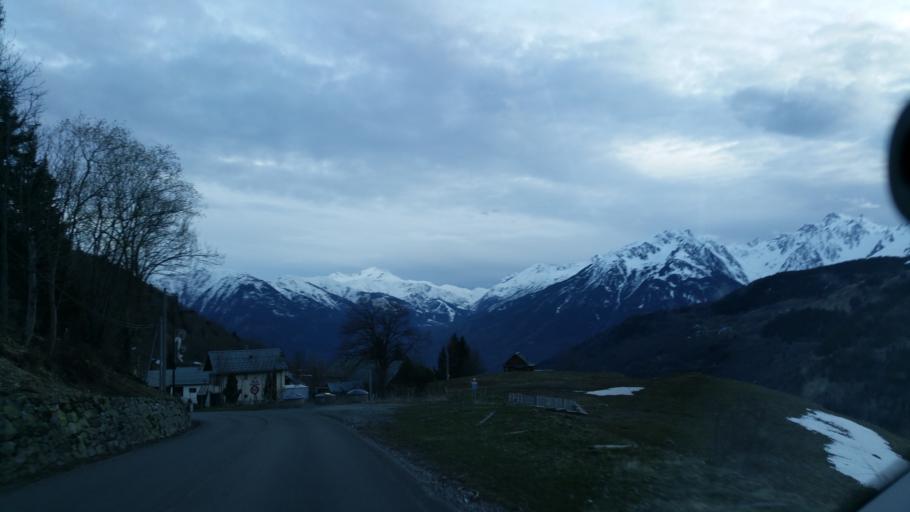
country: FR
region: Rhone-Alpes
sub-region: Departement de la Savoie
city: La Chambre
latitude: 45.4064
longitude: 6.3440
